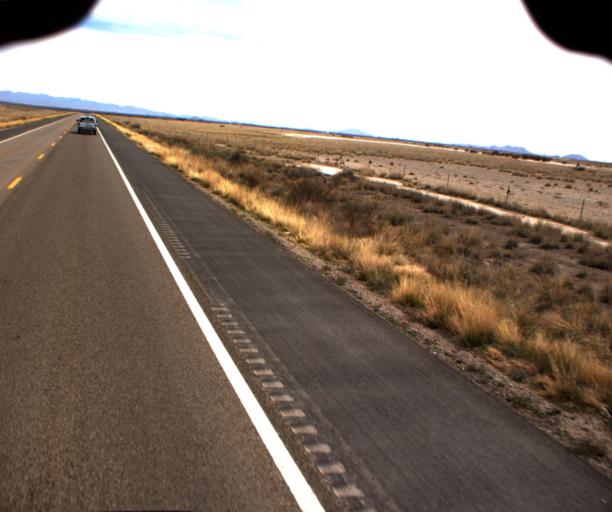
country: US
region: Arizona
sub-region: Cochise County
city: Willcox
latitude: 32.2086
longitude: -109.7756
